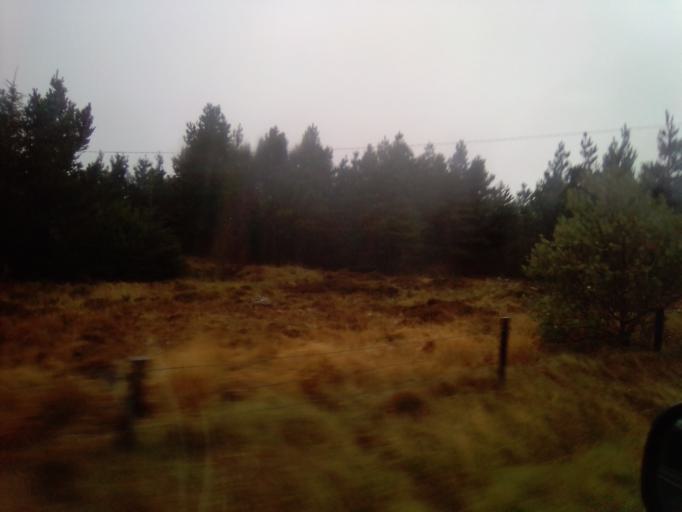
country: IE
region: Ulster
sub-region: County Donegal
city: Ramelton
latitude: 55.2621
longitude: -7.6390
